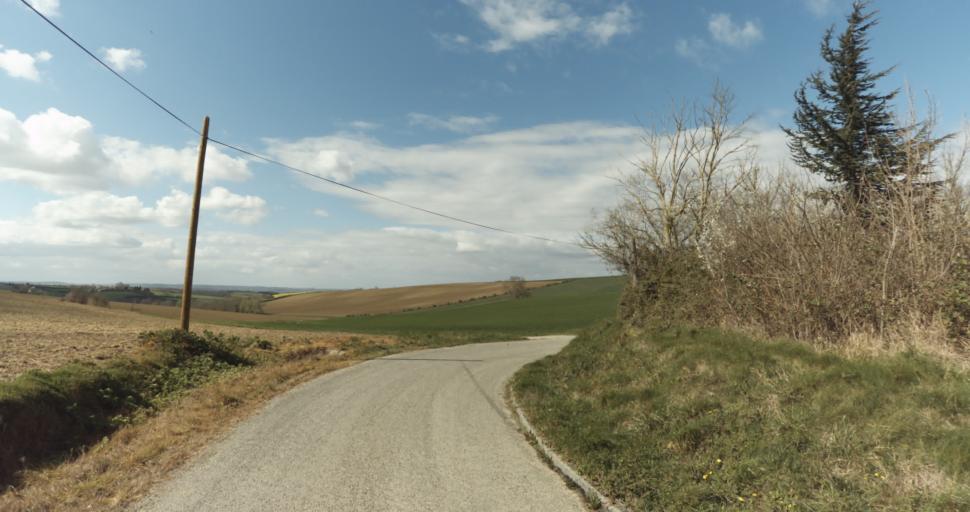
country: FR
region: Midi-Pyrenees
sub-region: Departement de la Haute-Garonne
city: Auterive
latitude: 43.3704
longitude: 1.5035
